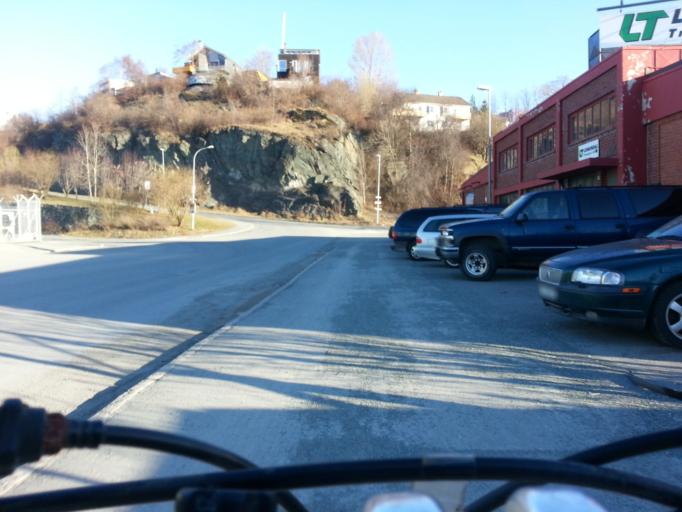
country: NO
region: Sor-Trondelag
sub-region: Trondheim
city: Trondheim
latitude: 63.4434
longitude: 10.4274
